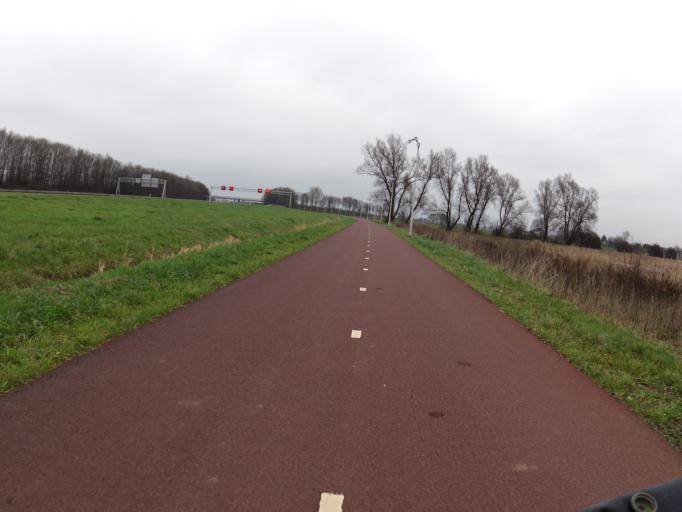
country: NL
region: Gelderland
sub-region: Gemeente Overbetuwe
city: Elst
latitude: 51.9011
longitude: 5.8716
